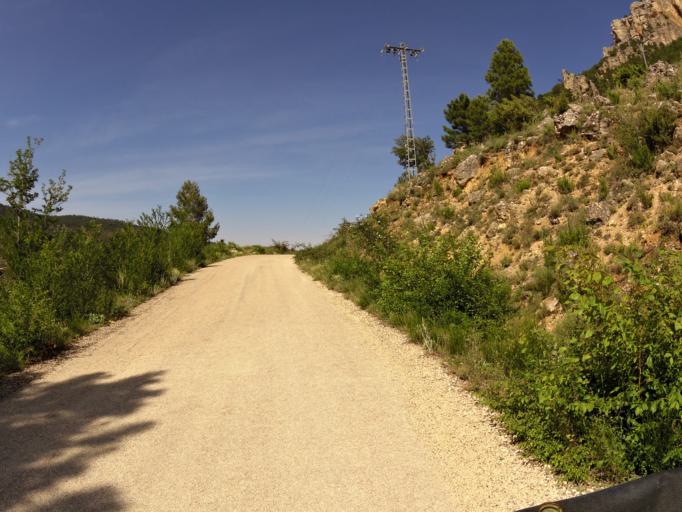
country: ES
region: Castille-La Mancha
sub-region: Provincia de Albacete
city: Paterna del Madera
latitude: 38.5812
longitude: -2.3179
